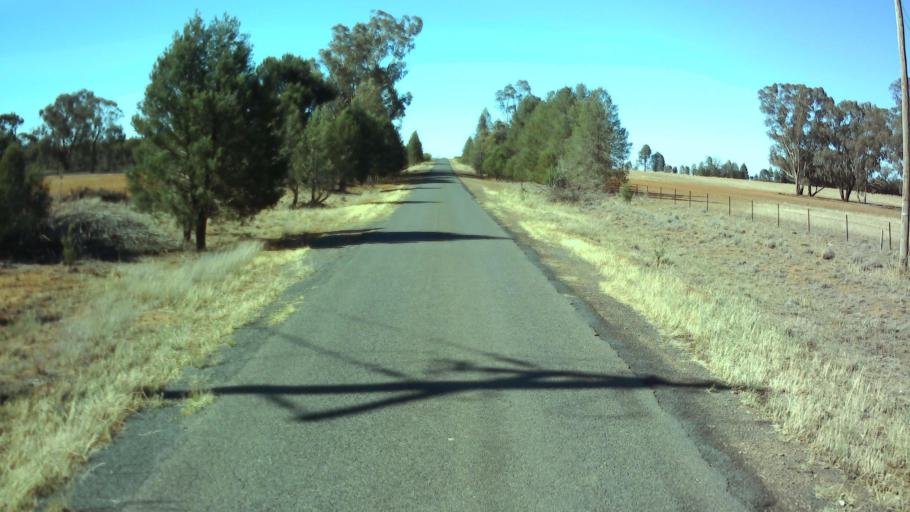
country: AU
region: New South Wales
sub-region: Weddin
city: Grenfell
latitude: -33.7584
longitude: 147.8299
